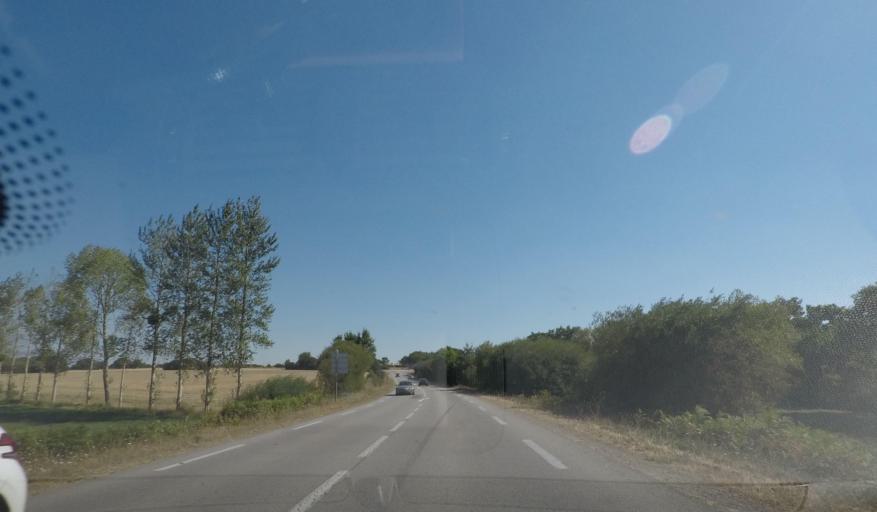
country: FR
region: Brittany
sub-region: Departement du Morbihan
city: Peaule
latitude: 47.5419
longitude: -2.3995
